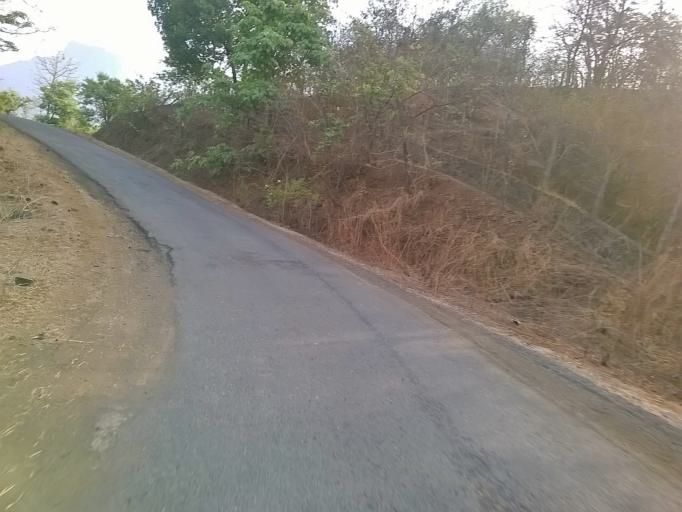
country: IN
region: Maharashtra
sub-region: Raigarh
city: Matheran
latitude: 19.0282
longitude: 73.2442
